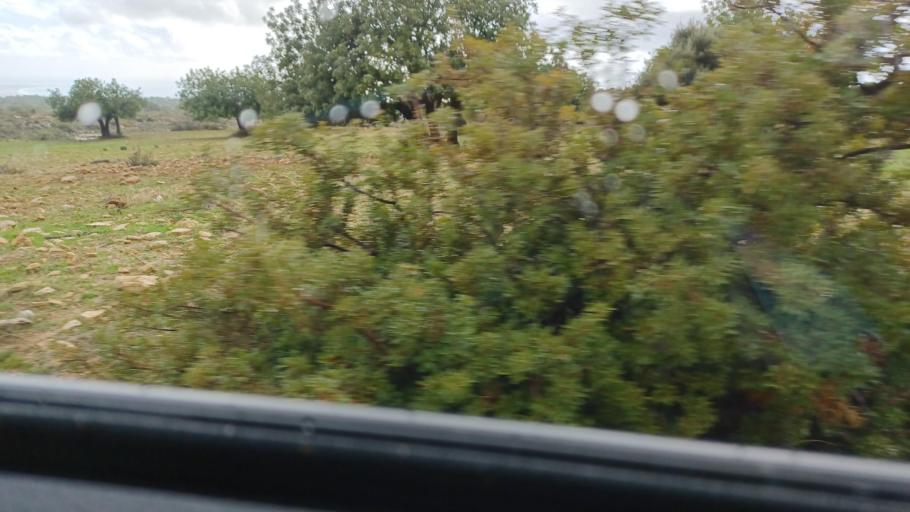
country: CY
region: Limassol
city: Sotira
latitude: 34.7435
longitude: 32.8577
